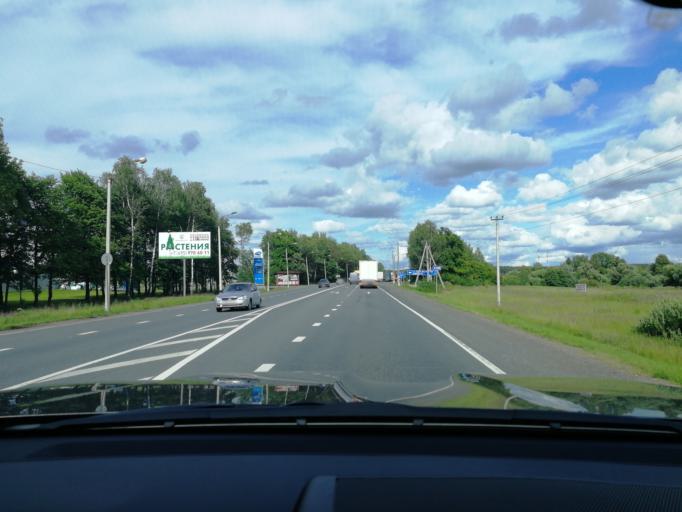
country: RU
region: Moskovskaya
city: Novyy Byt
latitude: 55.0376
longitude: 37.5749
